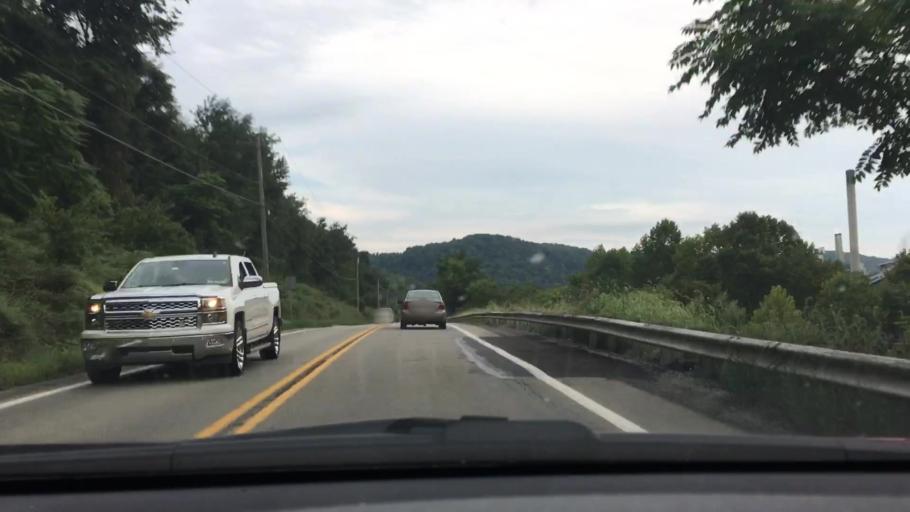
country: US
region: Pennsylvania
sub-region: Allegheny County
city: Wilson
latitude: 40.3106
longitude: -79.8755
